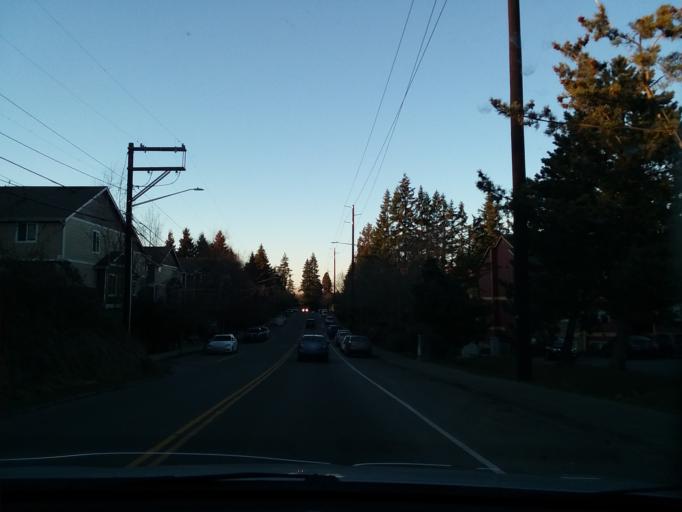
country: US
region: Washington
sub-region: Snohomish County
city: Mountlake Terrace
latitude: 47.8035
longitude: -122.2977
